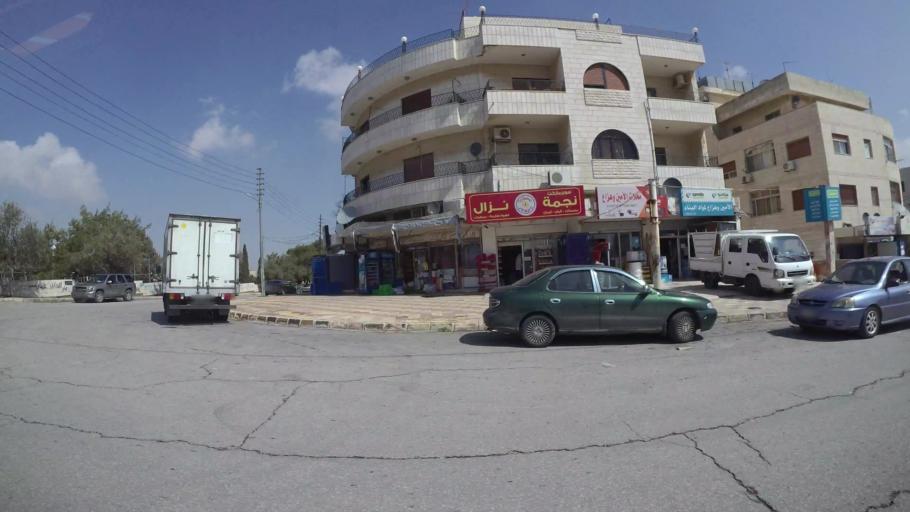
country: JO
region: Amman
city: Al Bunayyat ash Shamaliyah
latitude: 31.9262
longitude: 35.9016
